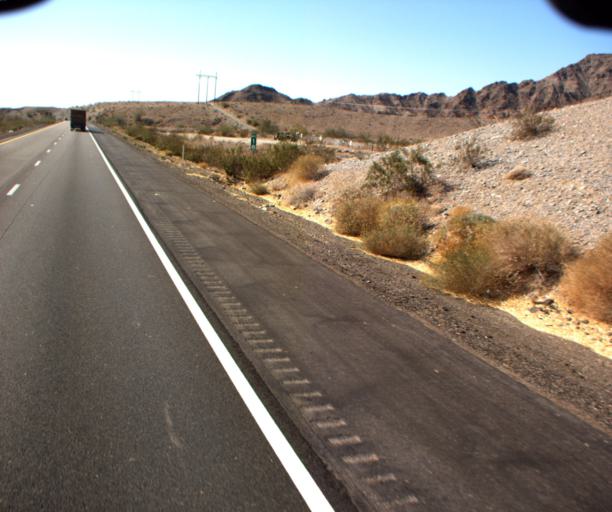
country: US
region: Arizona
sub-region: Yuma County
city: Fortuna Foothills
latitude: 32.6600
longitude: -114.3468
